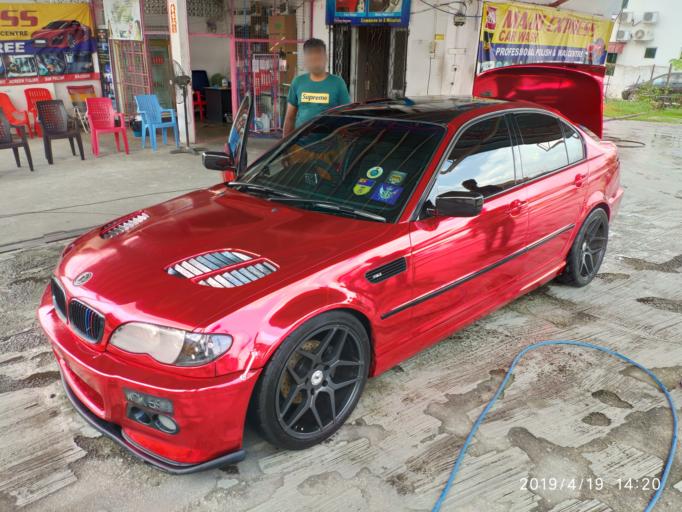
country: MY
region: Johor
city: Johor Bahru
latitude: 1.4852
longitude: 103.7716
